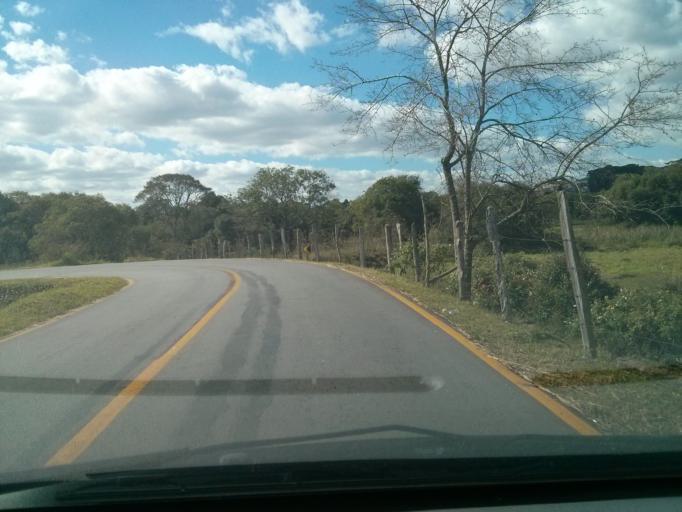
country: BR
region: Parana
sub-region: Sao Jose Dos Pinhais
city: Sao Jose dos Pinhais
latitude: -25.5600
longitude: -49.2264
